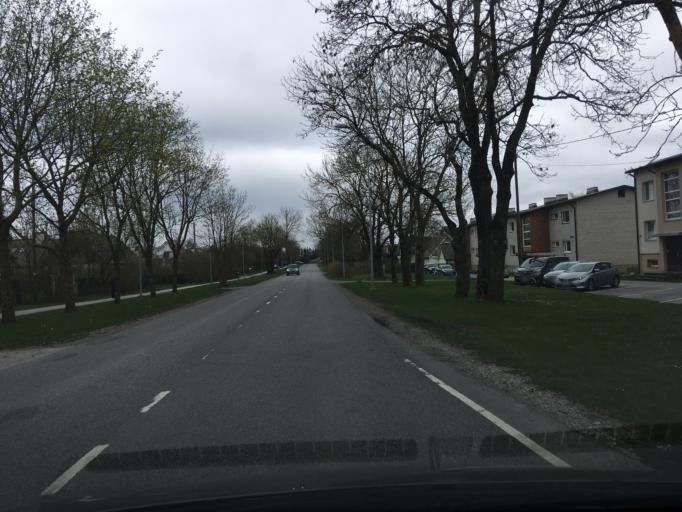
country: EE
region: Harju
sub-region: Rae vald
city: Jueri
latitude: 59.3539
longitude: 24.8940
